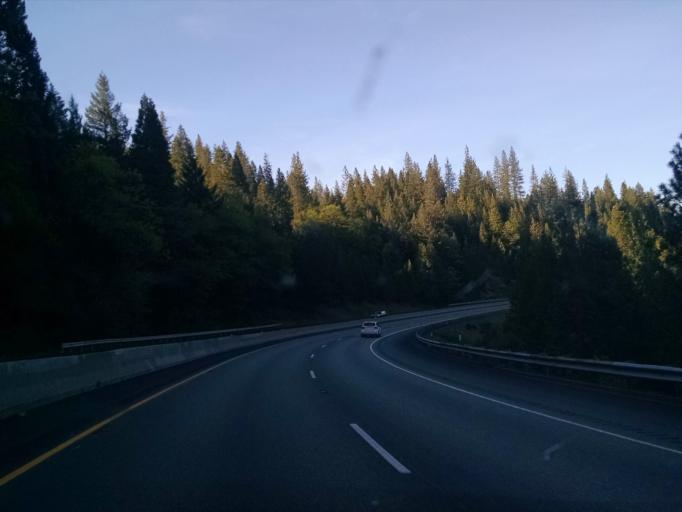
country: US
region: California
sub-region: Siskiyou County
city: Dunsmuir
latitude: 41.0897
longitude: -122.3528
